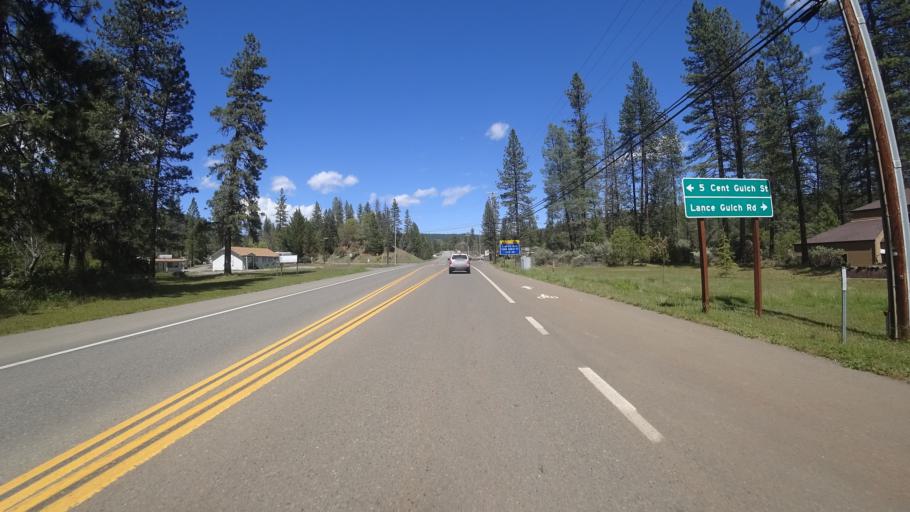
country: US
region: California
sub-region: Trinity County
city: Weaverville
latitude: 40.7387
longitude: -122.9277
